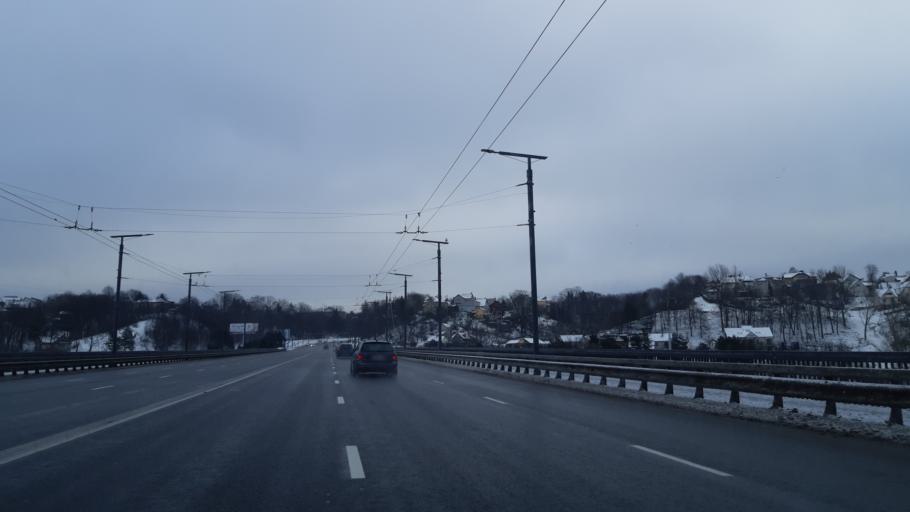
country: LT
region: Kauno apskritis
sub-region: Kaunas
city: Kaunas
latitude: 54.9144
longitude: 23.9083
